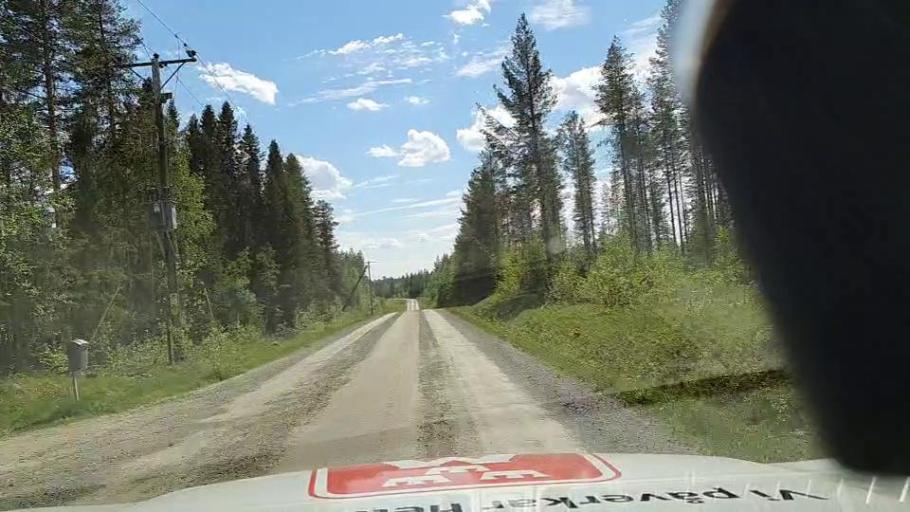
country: SE
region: Jaemtland
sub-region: Stroemsunds Kommun
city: Stroemsund
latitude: 64.4646
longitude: 15.5941
